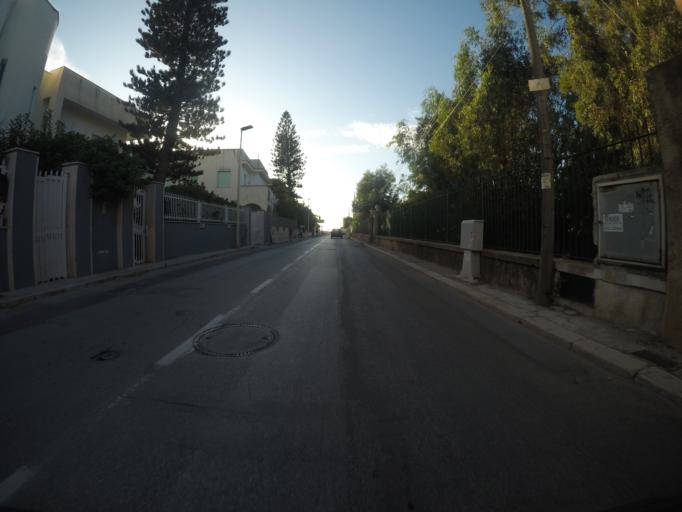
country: IT
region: Sicily
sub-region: Palermo
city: Isola delle Femmine
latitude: 38.1990
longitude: 13.2460
